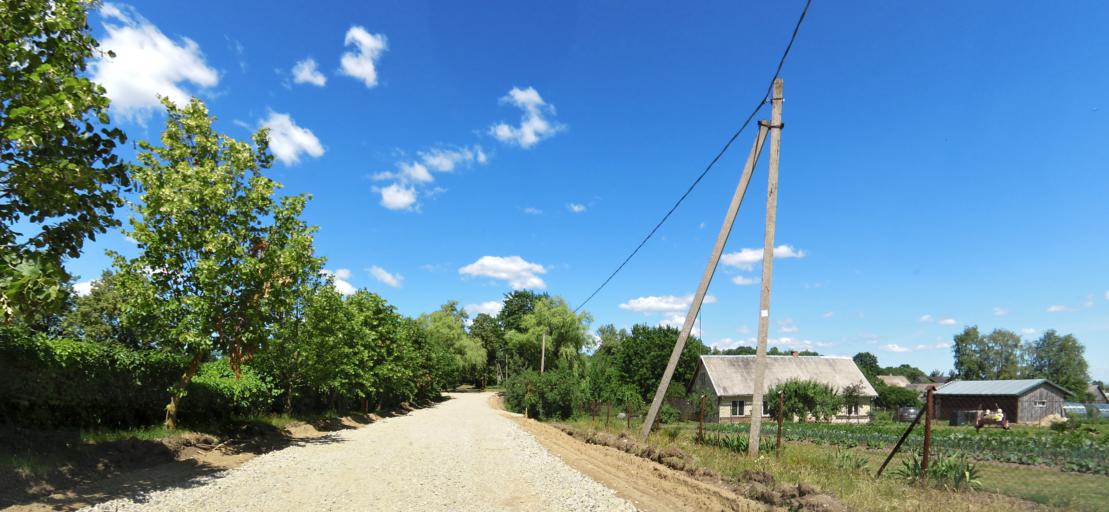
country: LT
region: Panevezys
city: Pasvalys
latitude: 56.2288
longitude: 24.4175
